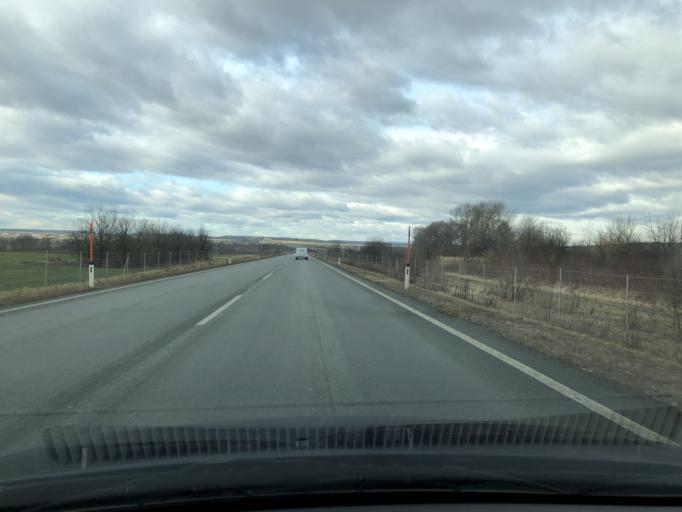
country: AT
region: Burgenland
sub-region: Politischer Bezirk Oberwart
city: Schachendorf
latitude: 47.2763
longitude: 16.4225
